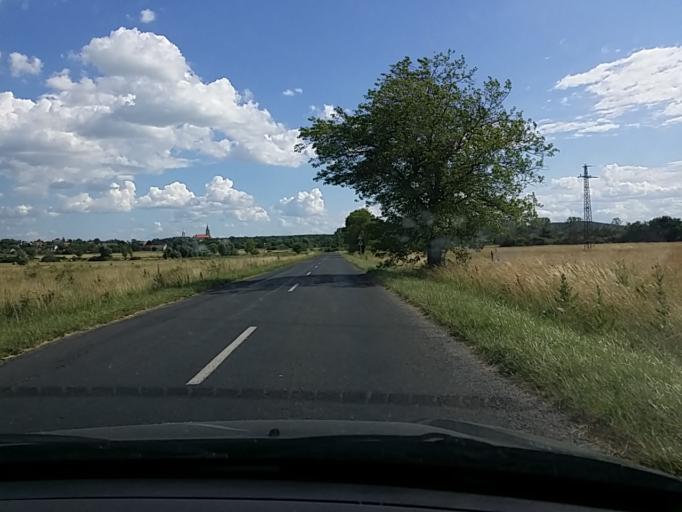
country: HU
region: Veszprem
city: Revfueloep
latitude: 46.8611
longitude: 17.6000
